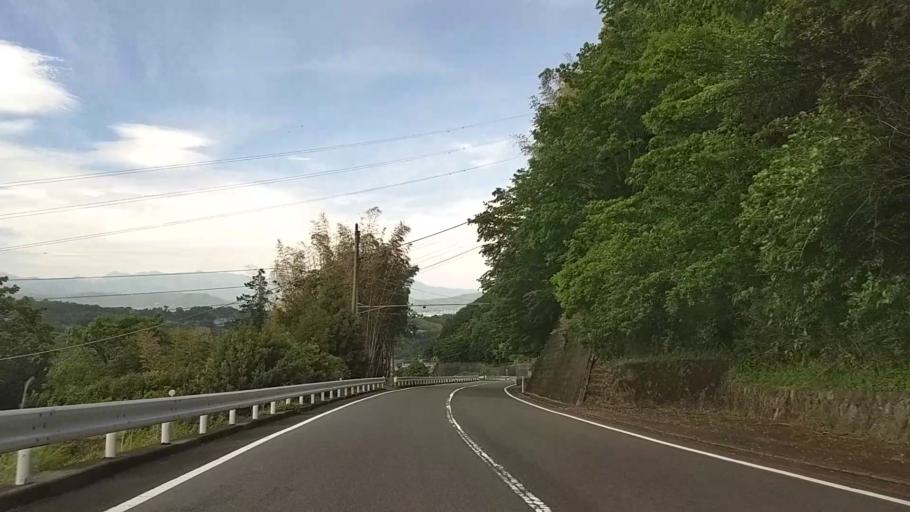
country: JP
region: Kanagawa
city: Odawara
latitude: 35.2393
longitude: 139.1281
